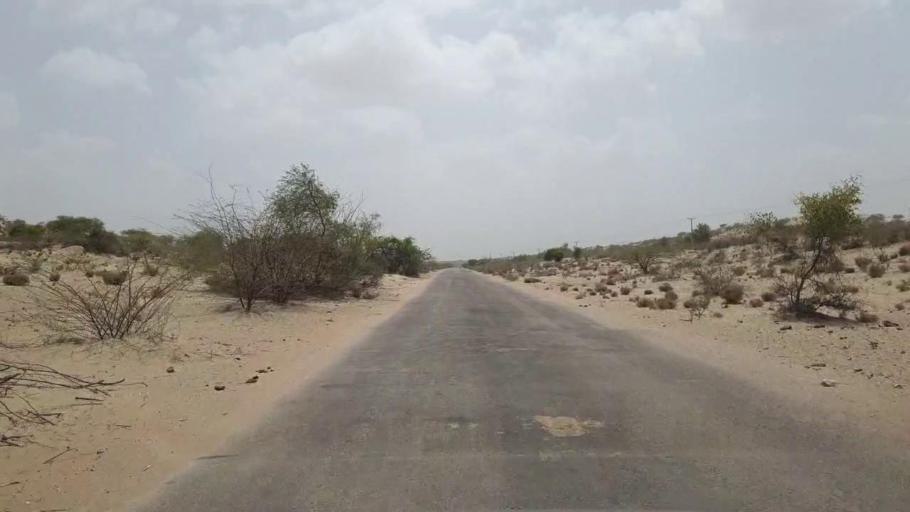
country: PK
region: Sindh
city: Diplo
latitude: 24.4047
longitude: 69.4778
